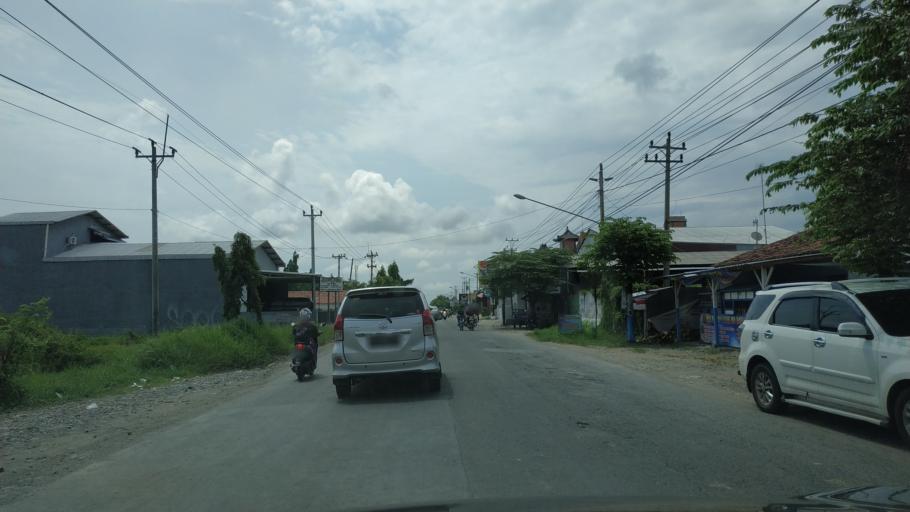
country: ID
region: Central Java
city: Adiwerna
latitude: -6.9244
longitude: 109.1259
